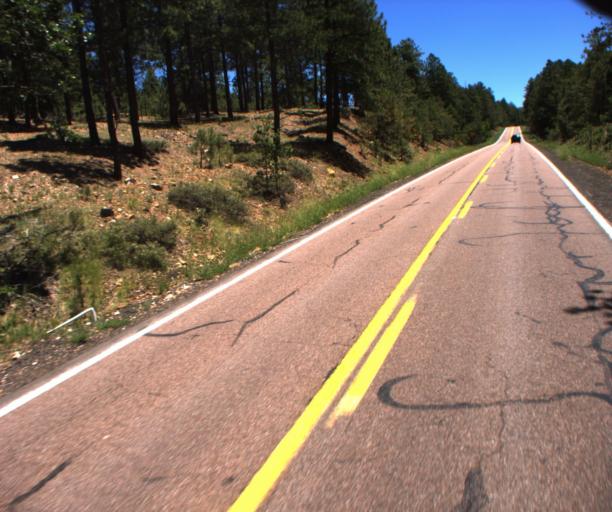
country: US
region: Arizona
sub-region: Gila County
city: Pine
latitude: 34.4534
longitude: -111.4340
